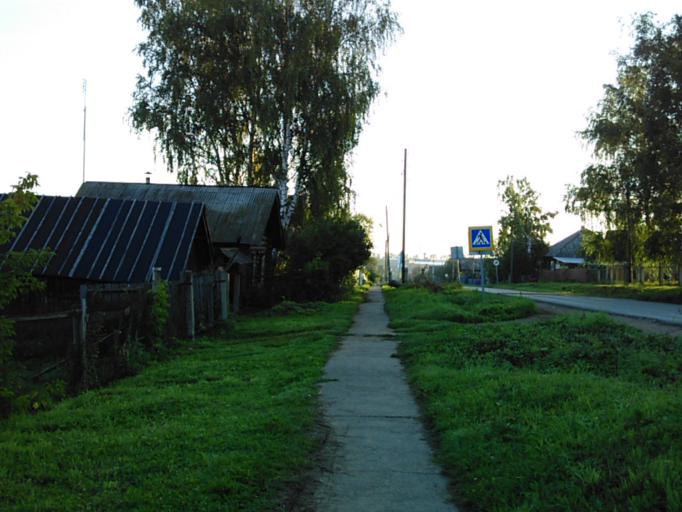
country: RU
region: Perm
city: Foki
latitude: 56.6941
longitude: 54.3500
